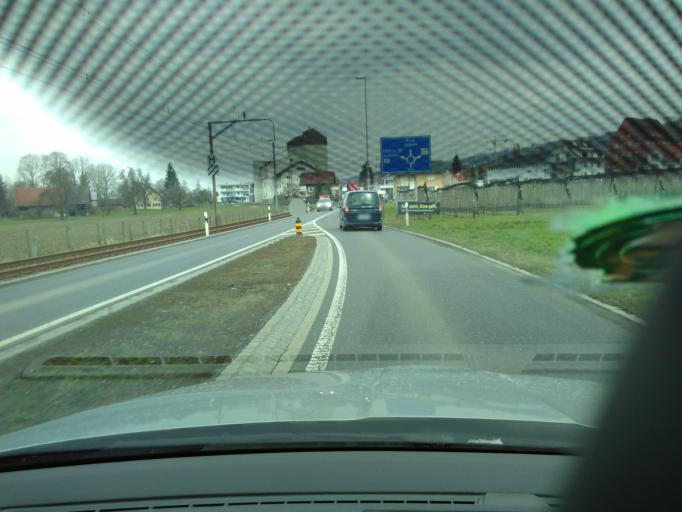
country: CH
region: Lucerne
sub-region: Hochdorf District
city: Hitzkirch
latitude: 47.2115
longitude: 8.2664
